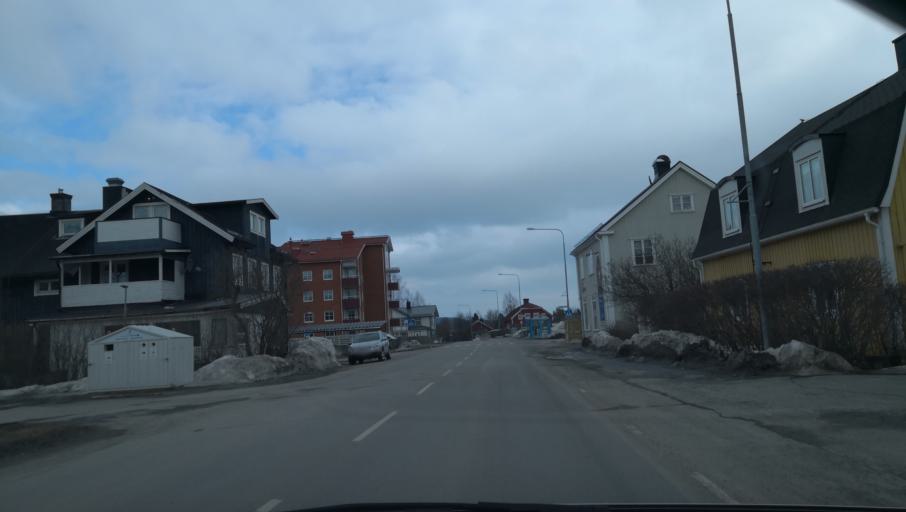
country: SE
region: Vaesterbotten
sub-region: Vannas Kommun
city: Vannasby
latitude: 63.9126
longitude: 19.8207
